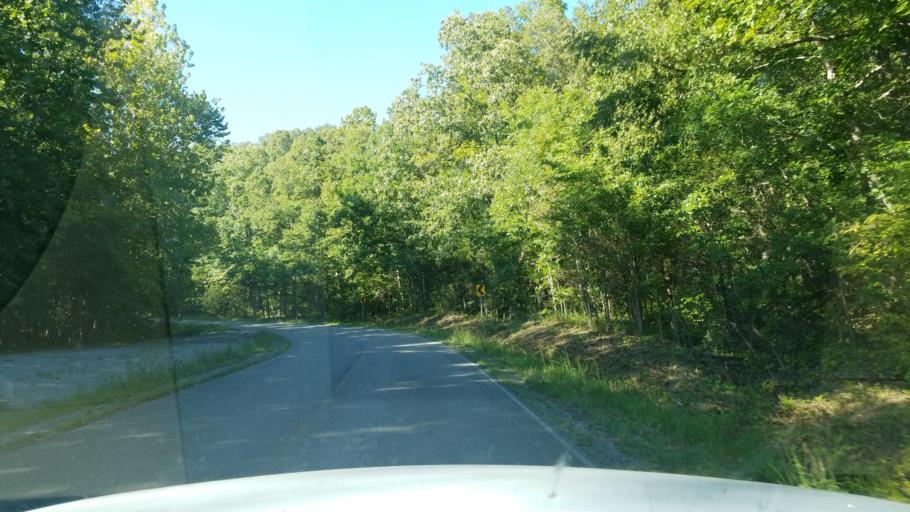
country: US
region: Illinois
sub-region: Hardin County
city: Elizabethtown
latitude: 37.5973
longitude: -88.3642
